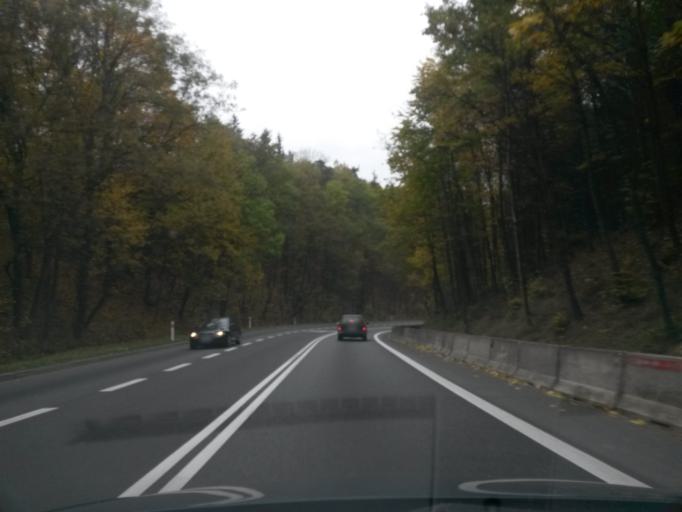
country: PL
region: Lower Silesian Voivodeship
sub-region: Powiat zabkowicki
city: Bardo
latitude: 50.4814
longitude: 16.7107
